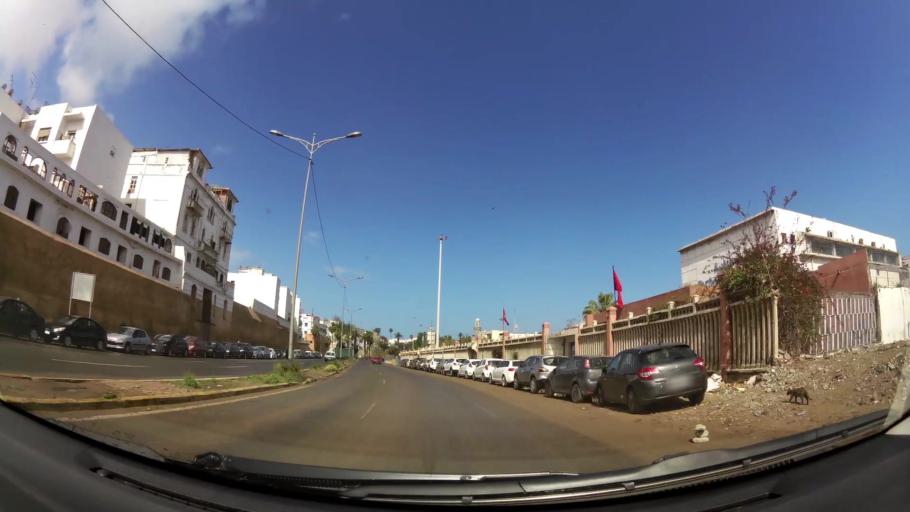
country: MA
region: Grand Casablanca
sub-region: Casablanca
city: Casablanca
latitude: 33.6004
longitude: -7.6149
